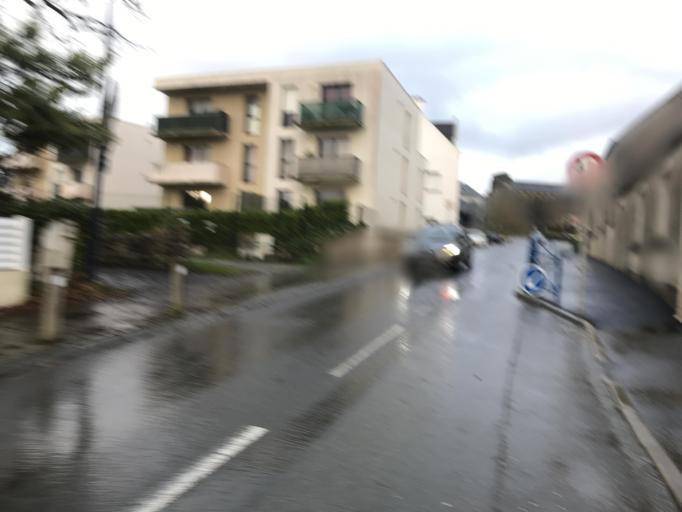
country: FR
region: Brittany
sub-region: Departement du Finistere
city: Loperhet
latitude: 48.3734
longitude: -4.3067
